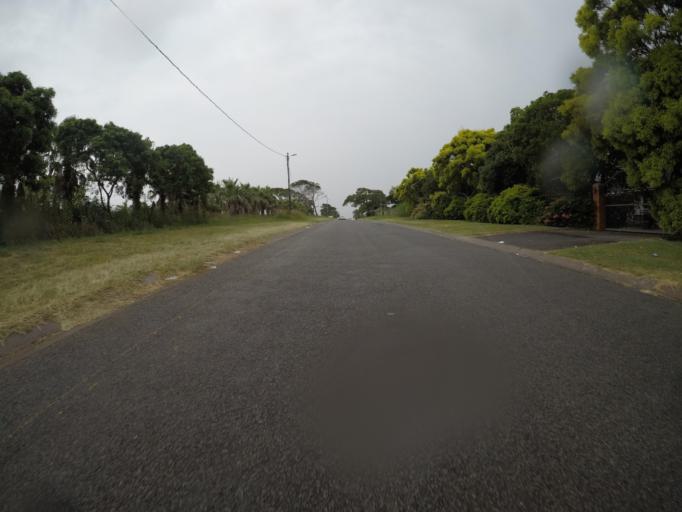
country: ZA
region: Eastern Cape
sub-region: Buffalo City Metropolitan Municipality
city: East London
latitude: -32.9853
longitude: 27.8587
